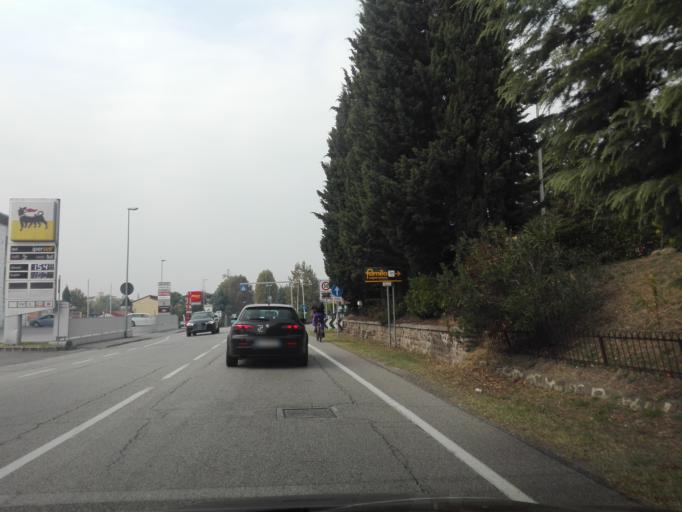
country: IT
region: Veneto
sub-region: Provincia di Verona
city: Cavalcaselle
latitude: 45.4421
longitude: 10.7059
